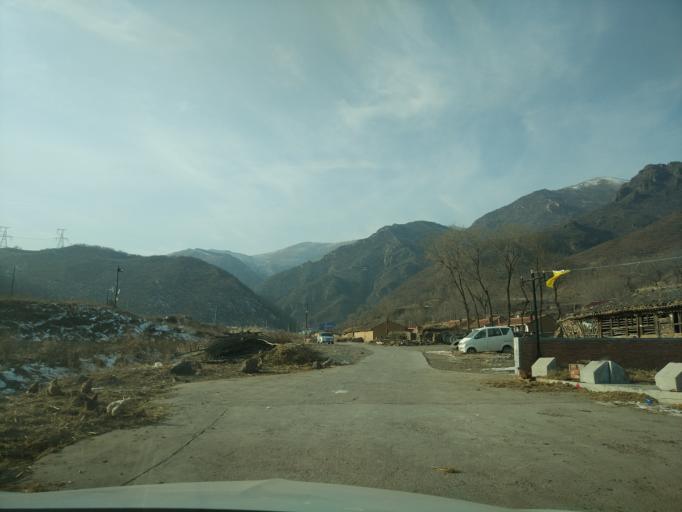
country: CN
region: Hebei
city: Xiwanzi
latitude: 40.8148
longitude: 115.4590
